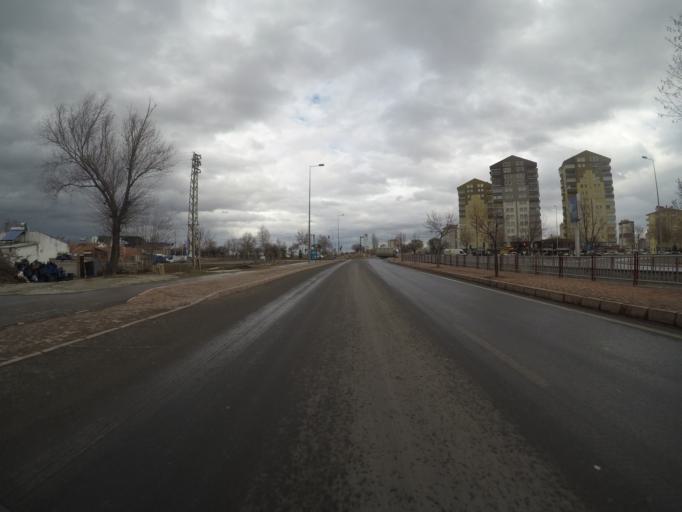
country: TR
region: Kayseri
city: Kayseri
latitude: 38.7580
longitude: 35.4817
